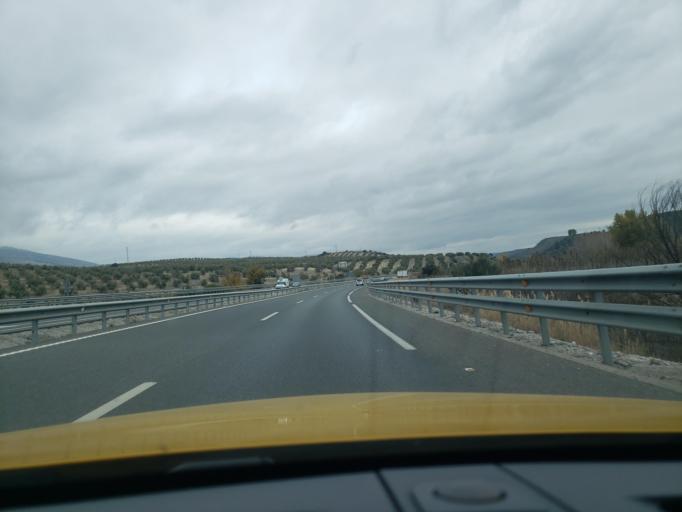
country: ES
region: Andalusia
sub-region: Provincia de Granada
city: Calicasas
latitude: 37.3047
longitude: -3.6581
